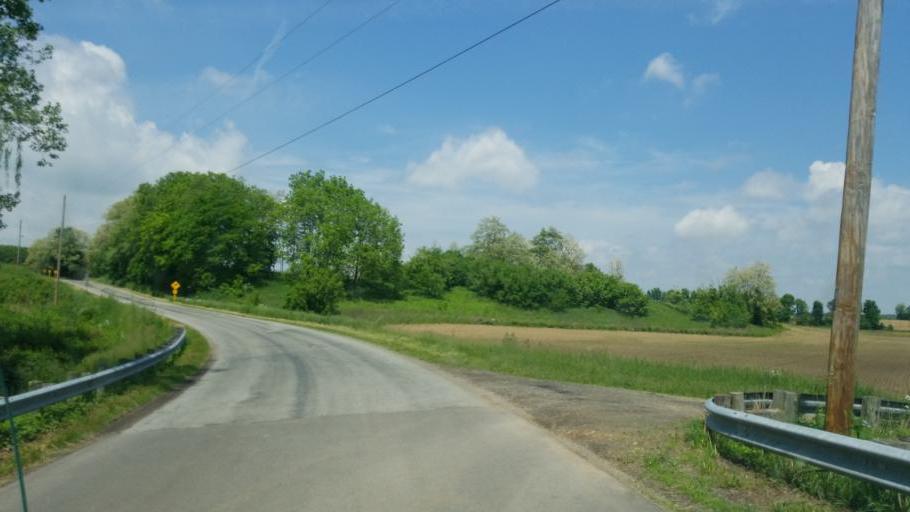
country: US
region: Ohio
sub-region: Ashland County
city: Ashland
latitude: 40.8346
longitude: -82.2509
